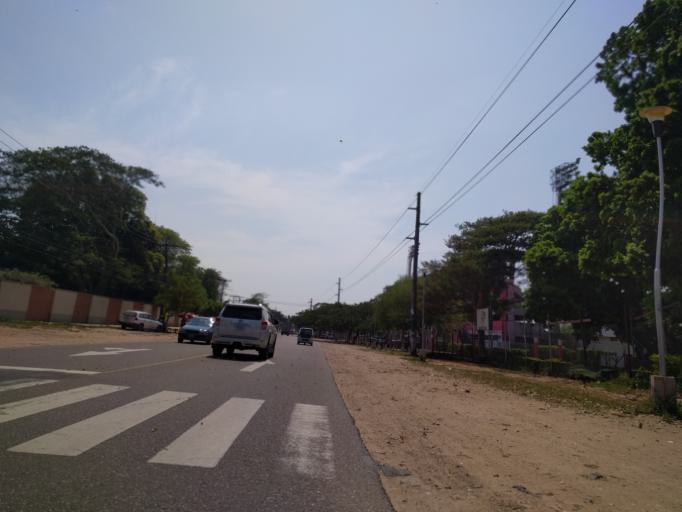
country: BO
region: Santa Cruz
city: Santa Cruz de la Sierra
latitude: -17.8056
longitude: -63.1674
